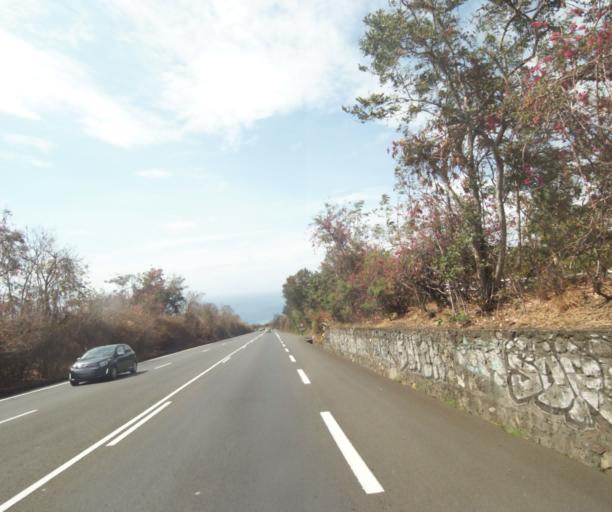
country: RE
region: Reunion
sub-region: Reunion
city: Saint-Paul
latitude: -21.0247
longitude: 55.2739
